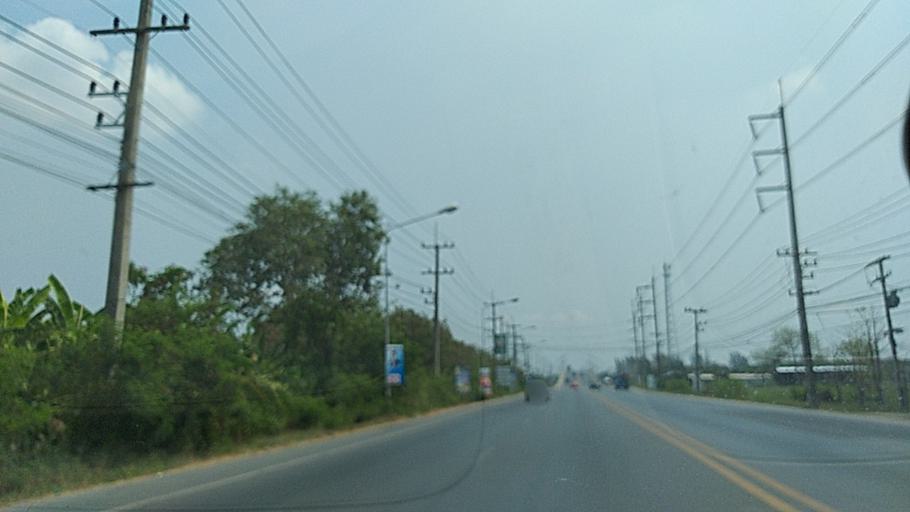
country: TH
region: Bangkok
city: Nong Chok
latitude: 13.9605
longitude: 100.8906
